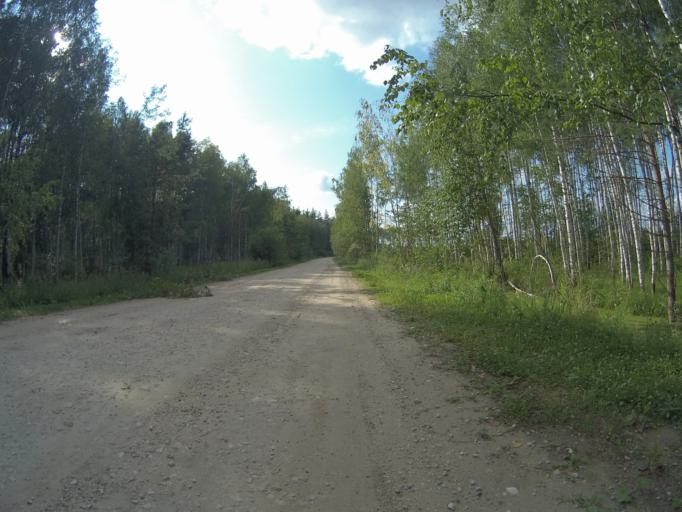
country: RU
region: Vladimir
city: Orgtrud
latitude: 56.3079
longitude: 40.7616
